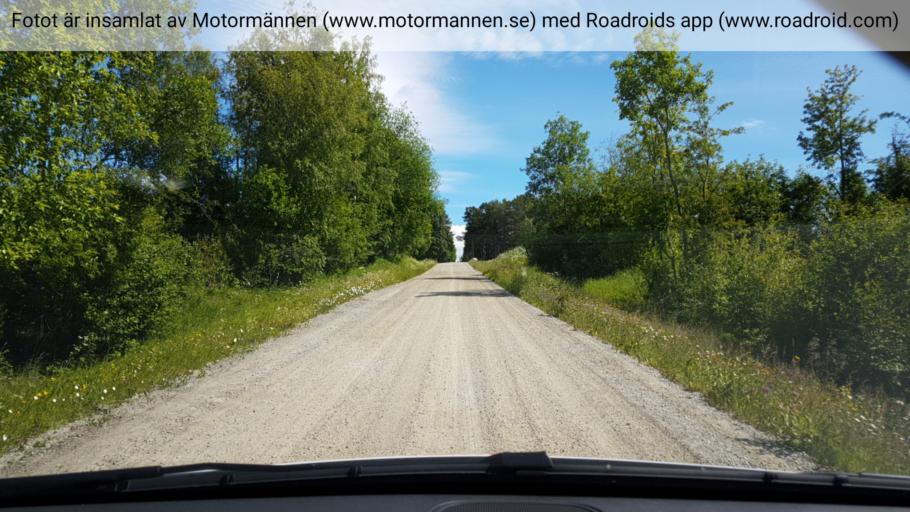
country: SE
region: Jaemtland
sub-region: Bergs Kommun
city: Hoverberg
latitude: 62.8958
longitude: 14.5282
